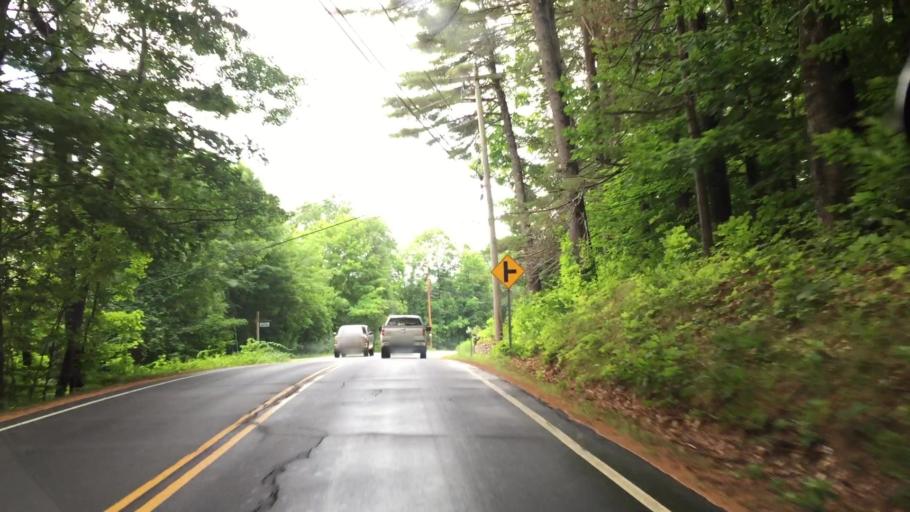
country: US
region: New Hampshire
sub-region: Grafton County
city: Holderness
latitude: 43.7485
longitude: -71.5580
